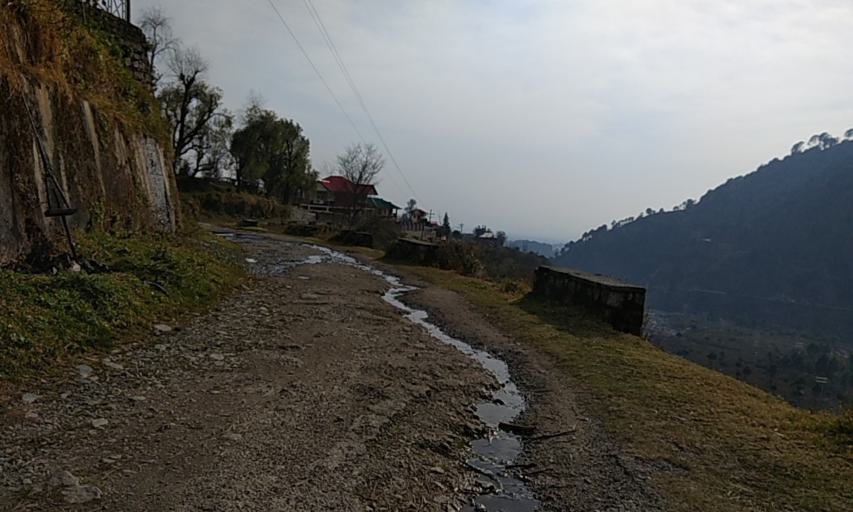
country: IN
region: Himachal Pradesh
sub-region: Kangra
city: Palampur
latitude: 32.1404
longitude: 76.5377
